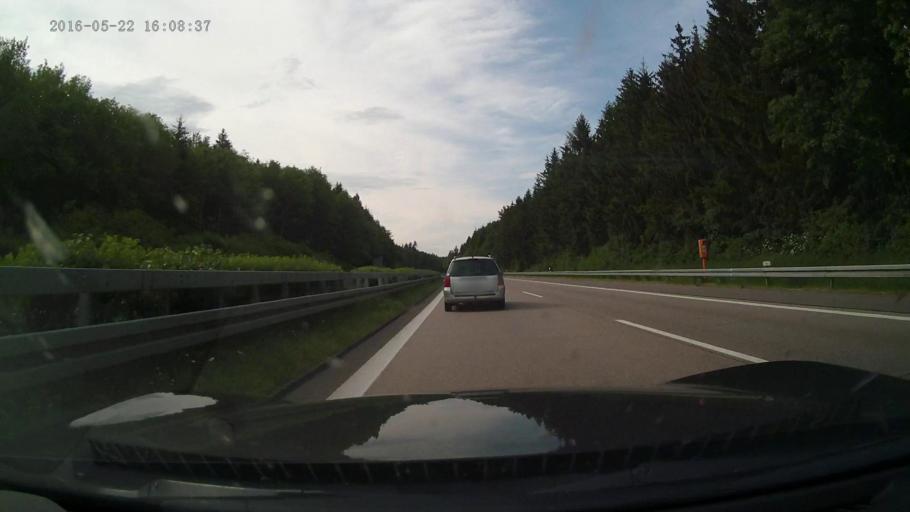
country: DE
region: Baden-Wuerttemberg
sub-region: Regierungsbezirk Stuttgart
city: Widdern
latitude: 49.3326
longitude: 9.4116
